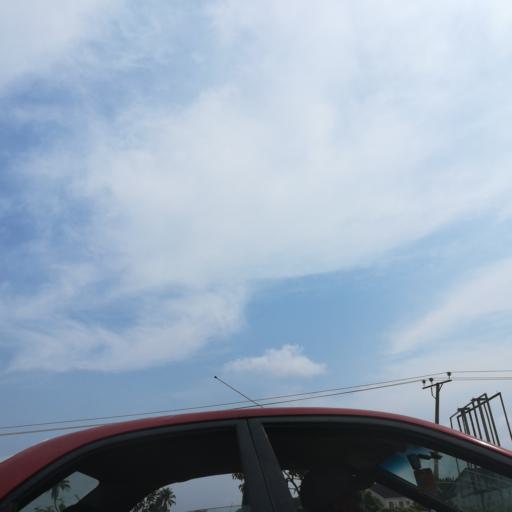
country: NG
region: Rivers
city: Port Harcourt
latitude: 4.8543
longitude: 7.0218
